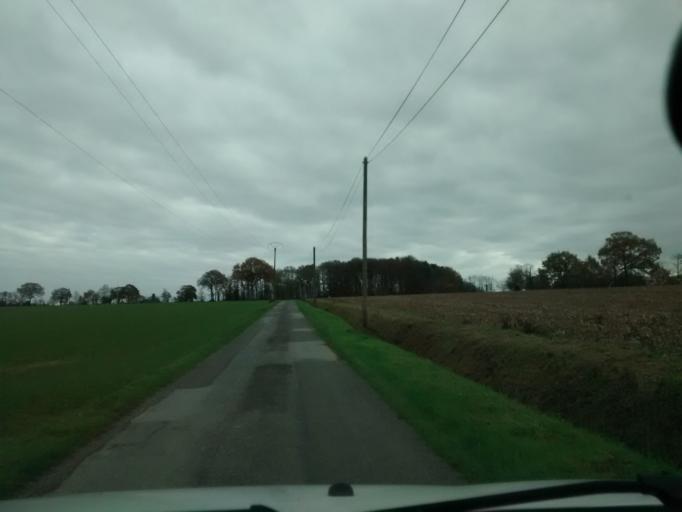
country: FR
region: Brittany
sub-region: Departement d'Ille-et-Vilaine
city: Erbree
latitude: 48.0905
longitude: -1.1552
